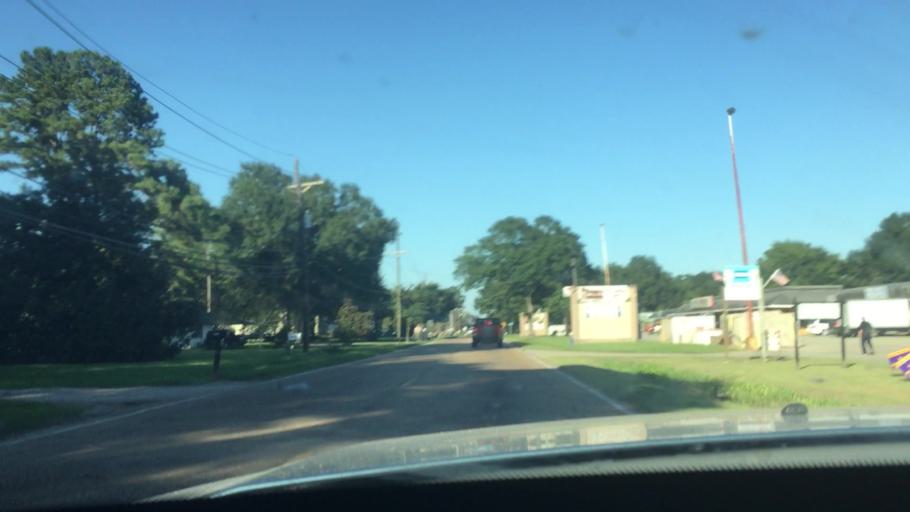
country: US
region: Louisiana
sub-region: East Baton Rouge Parish
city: Monticello
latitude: 30.4559
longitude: -91.0165
